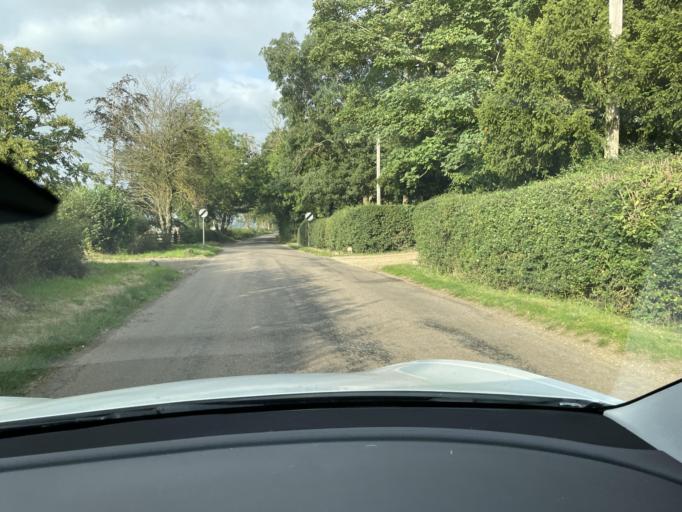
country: GB
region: England
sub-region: Northamptonshire
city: Brixworth
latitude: 52.3912
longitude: -0.9521
